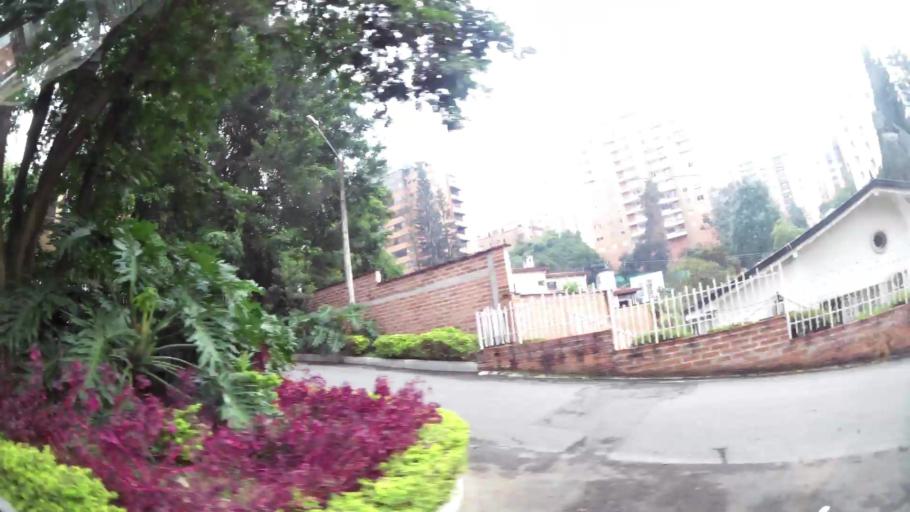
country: CO
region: Antioquia
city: Medellin
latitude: 6.2151
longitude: -75.5653
